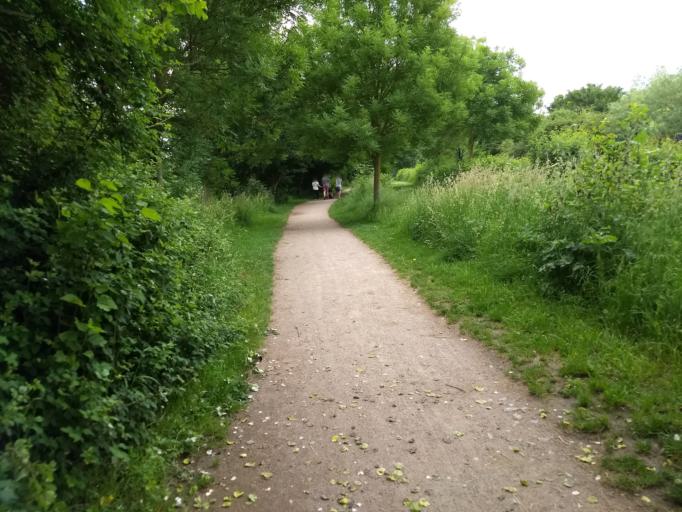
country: GB
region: England
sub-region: Central Bedfordshire
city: Marston Moretaine
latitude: 52.0646
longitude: -0.5380
